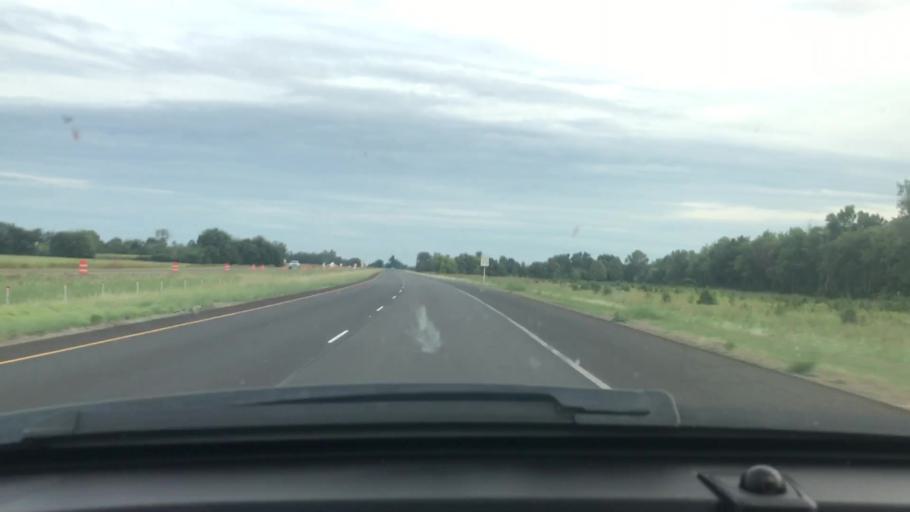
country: US
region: Arkansas
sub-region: Poinsett County
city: Trumann
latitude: 35.6704
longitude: -90.5528
